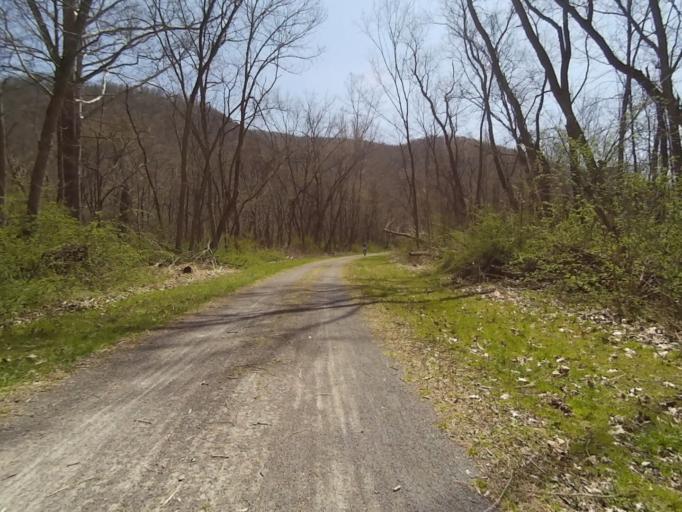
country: US
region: Pennsylvania
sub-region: Blair County
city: Williamsburg
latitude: 40.5078
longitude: -78.1652
